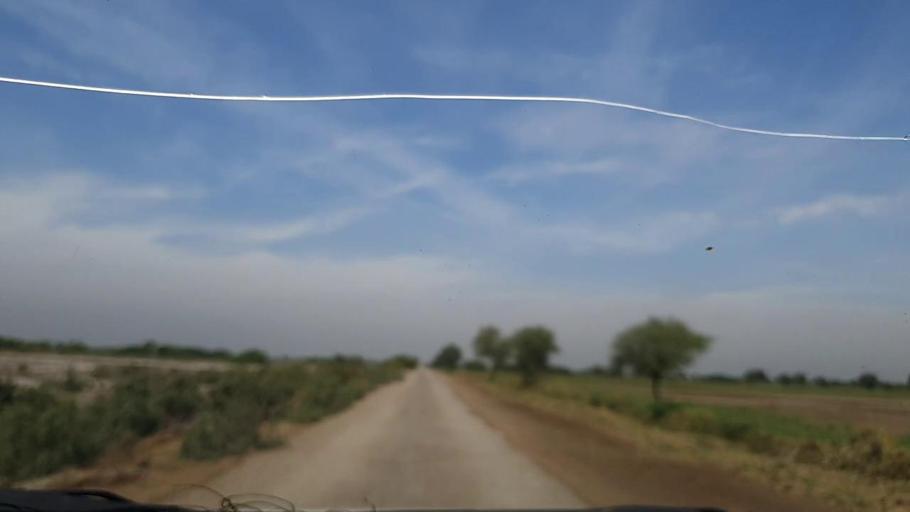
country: PK
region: Sindh
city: Pithoro
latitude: 25.4798
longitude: 69.4555
